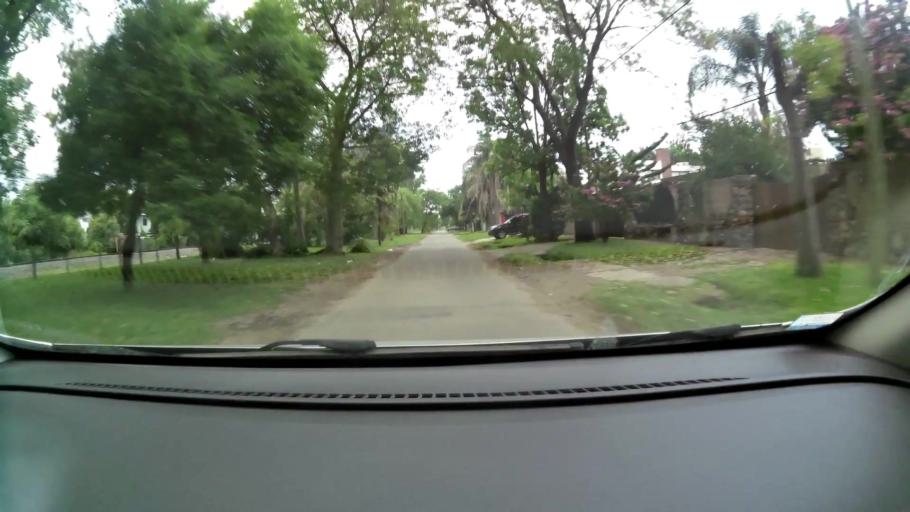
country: AR
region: Santa Fe
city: Granadero Baigorria
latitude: -32.8804
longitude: -60.7037
